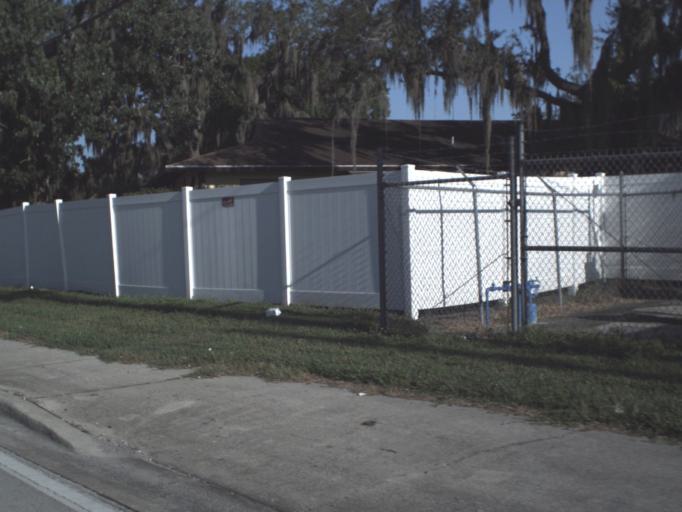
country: US
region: Florida
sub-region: Polk County
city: Jan-Phyl Village
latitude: 28.0053
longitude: -81.7852
